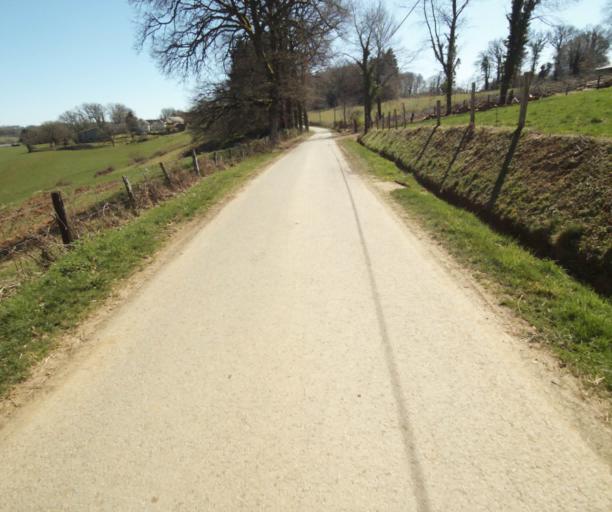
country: FR
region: Limousin
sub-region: Departement de la Correze
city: Chamboulive
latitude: 45.3991
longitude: 1.6373
